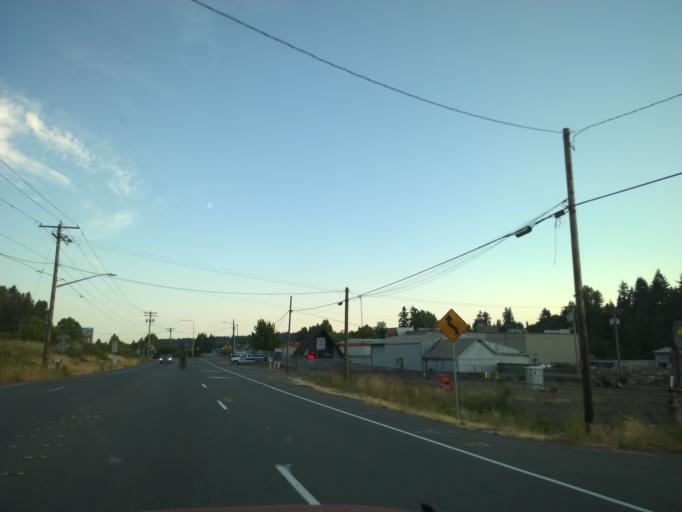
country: US
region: Washington
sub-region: King County
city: Woodinville
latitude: 47.7668
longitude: -122.1545
